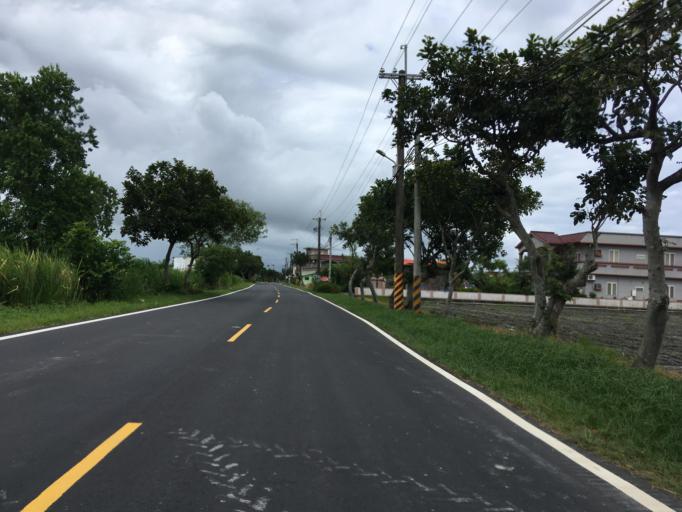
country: TW
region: Taiwan
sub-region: Yilan
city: Yilan
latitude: 24.6854
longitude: 121.8086
